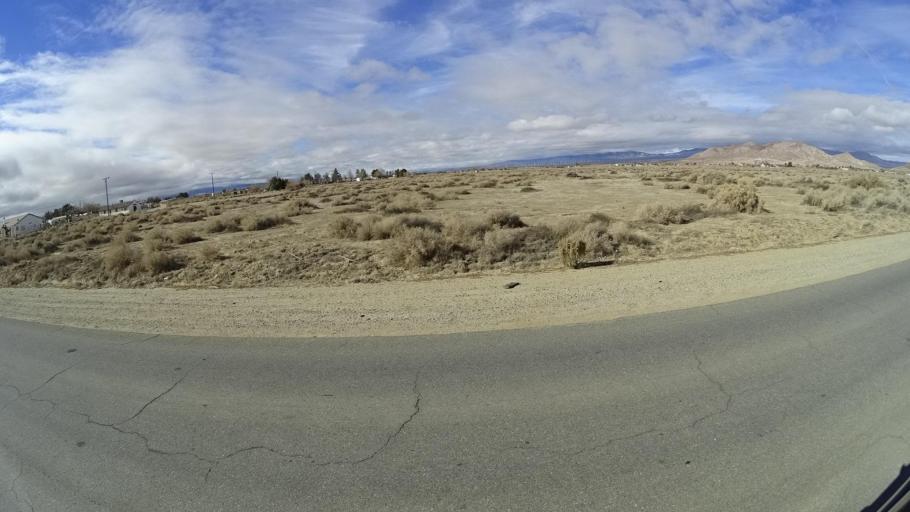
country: US
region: California
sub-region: Kern County
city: Rosamond
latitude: 34.8531
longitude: -118.2379
